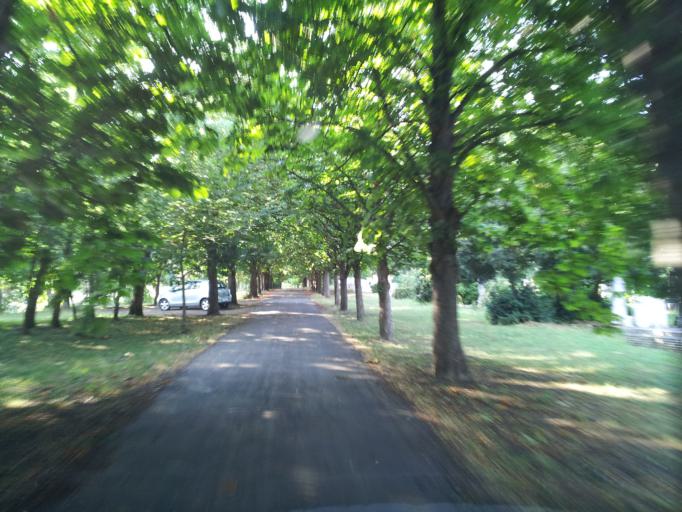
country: HU
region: Fejer
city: Lajoskomarom
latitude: 46.8366
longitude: 18.3364
